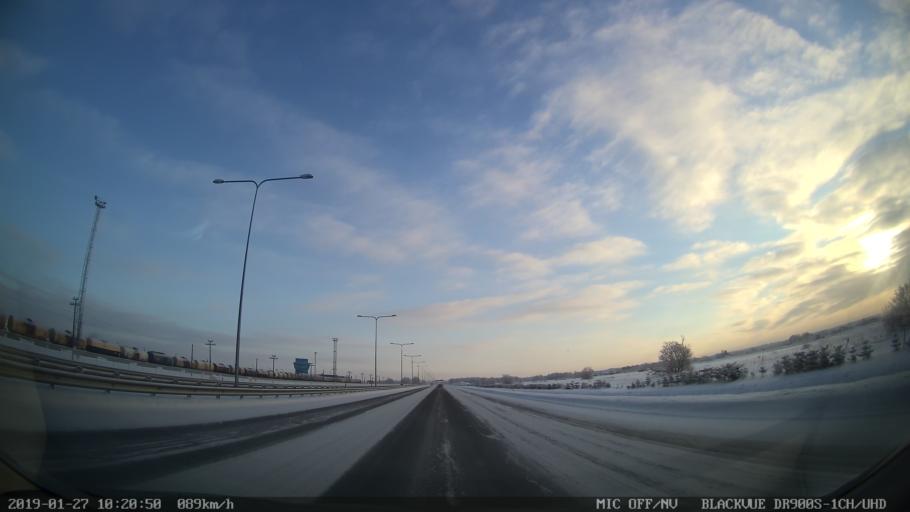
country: EE
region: Harju
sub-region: Joelaehtme vald
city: Loo
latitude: 59.4486
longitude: 24.9532
